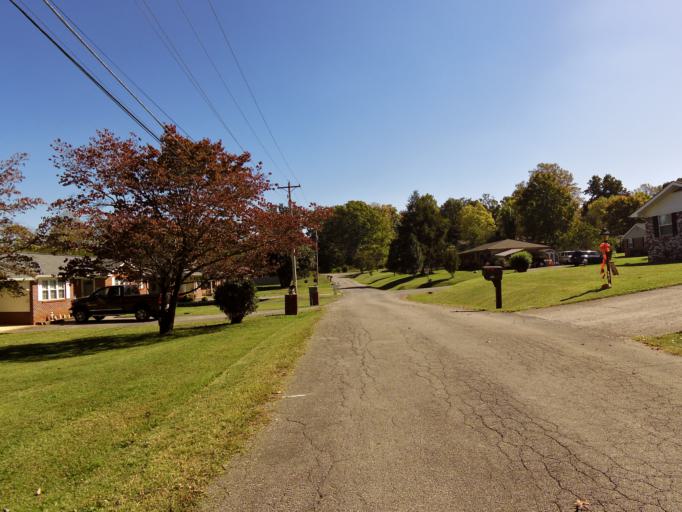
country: US
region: Tennessee
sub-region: Blount County
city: Eagleton Village
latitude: 35.8035
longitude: -83.9478
